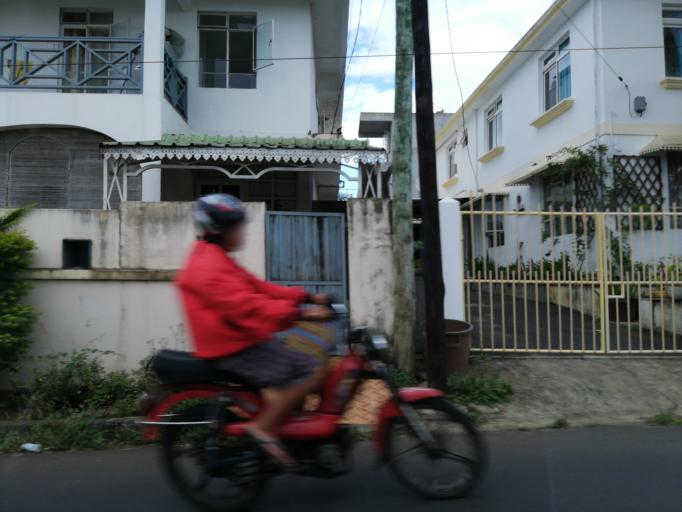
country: MU
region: Black River
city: Gros Cailloux
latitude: -20.2344
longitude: 57.4534
